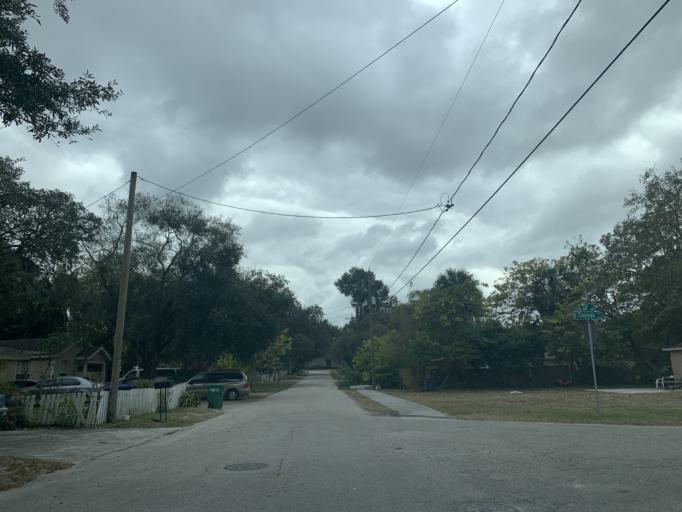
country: US
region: Florida
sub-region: Hillsborough County
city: East Lake-Orient Park
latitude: 27.9866
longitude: -82.4085
